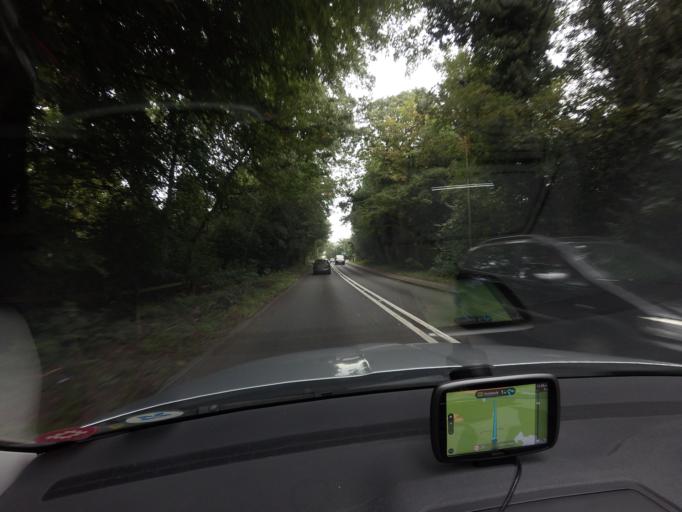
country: GB
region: England
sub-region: Surrey
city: Byfleet
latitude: 51.3380
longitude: -0.4471
